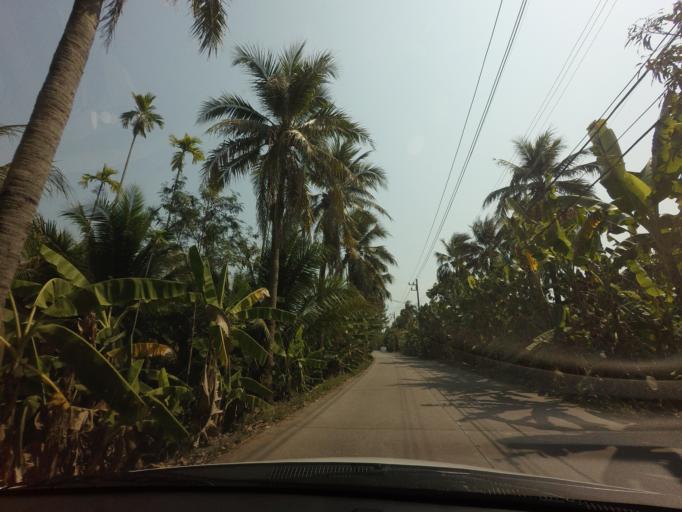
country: TH
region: Nakhon Pathom
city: Sam Phran
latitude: 13.7559
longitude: 100.2605
